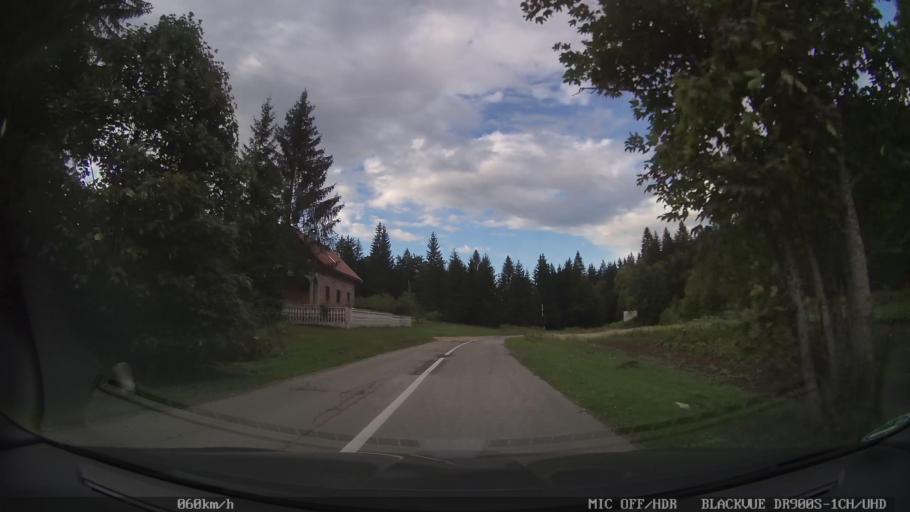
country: HR
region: Licko-Senjska
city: Jezerce
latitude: 44.9586
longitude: 15.5256
